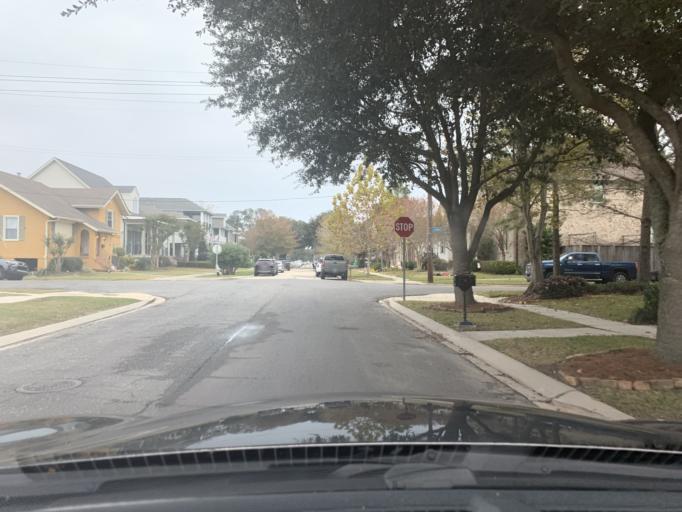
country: US
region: Louisiana
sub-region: Jefferson Parish
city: Metairie
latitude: 30.0139
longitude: -90.1082
